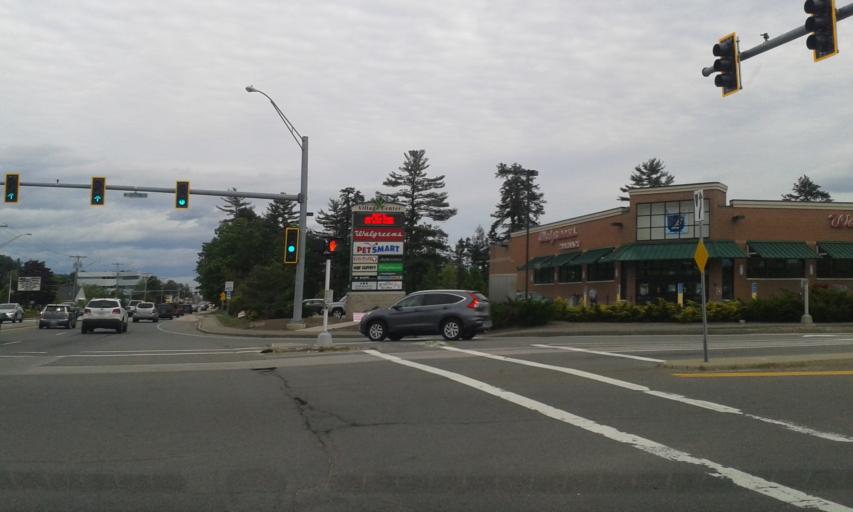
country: US
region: New Hampshire
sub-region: Hillsborough County
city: Litchfield
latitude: 42.7990
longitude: -71.5337
